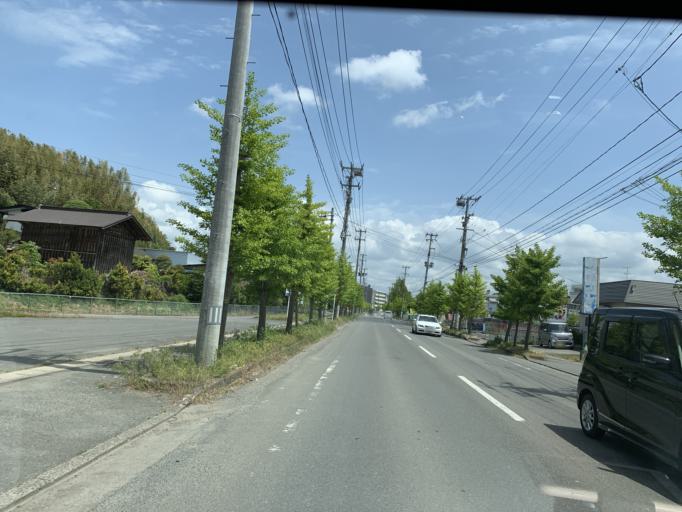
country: JP
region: Miyagi
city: Wakuya
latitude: 38.6914
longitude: 141.1849
